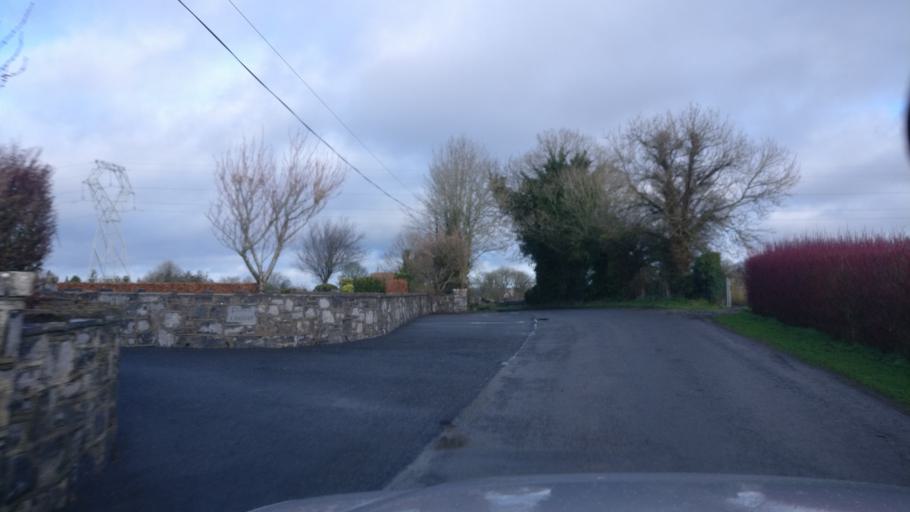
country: IE
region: Connaught
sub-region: County Galway
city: Loughrea
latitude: 53.2154
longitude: -8.5439
